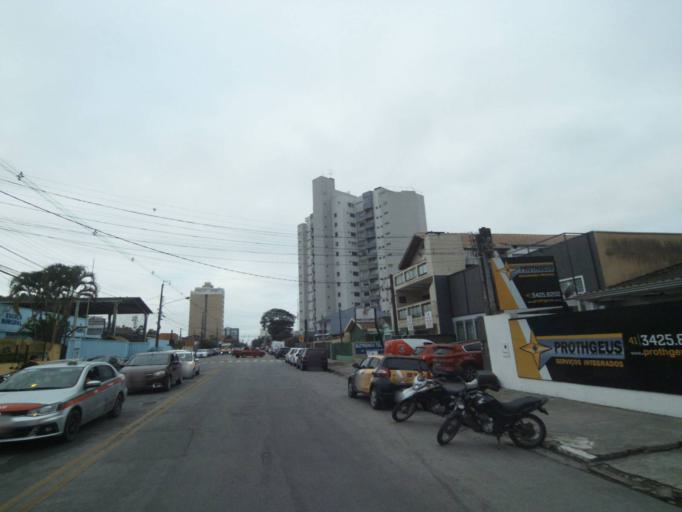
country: BR
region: Parana
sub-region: Paranagua
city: Paranagua
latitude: -25.5200
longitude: -48.5137
